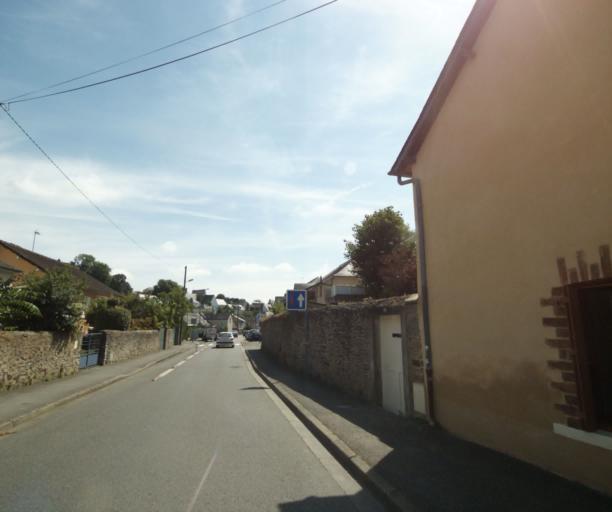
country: FR
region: Pays de la Loire
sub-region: Departement de la Mayenne
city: Laval
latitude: 48.0628
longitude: -0.7748
